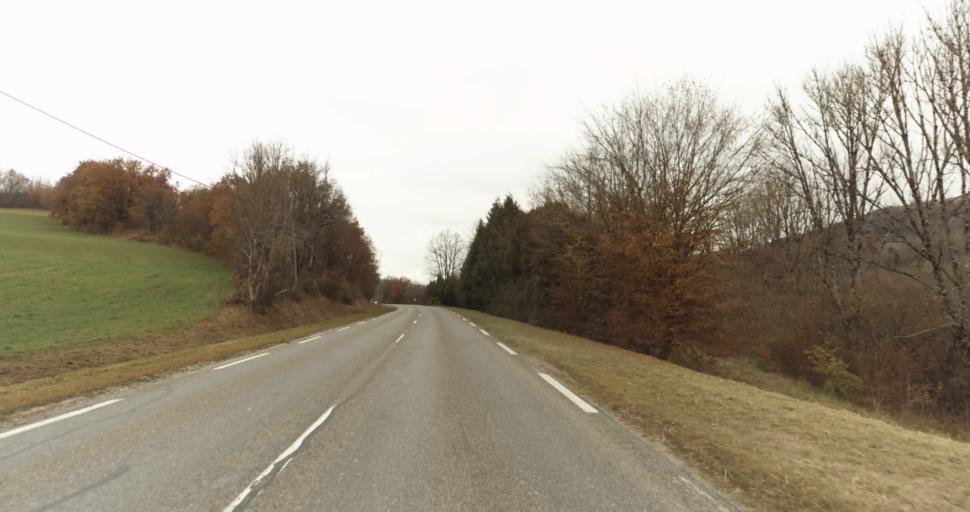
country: FR
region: Rhone-Alpes
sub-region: Departement de la Haute-Savoie
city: Saint-Martin-Bellevue
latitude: 45.9863
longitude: 6.1679
